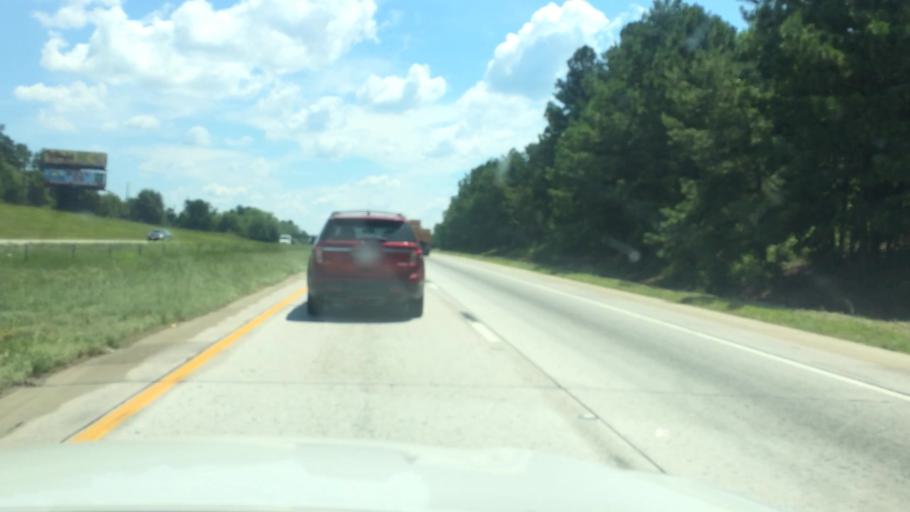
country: US
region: South Carolina
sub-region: Aiken County
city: Belvedere
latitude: 33.5475
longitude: -81.9621
